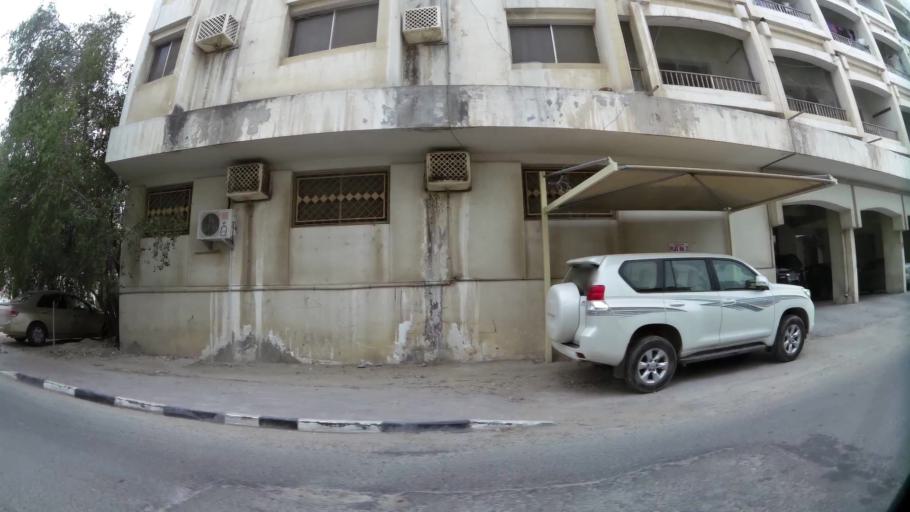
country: QA
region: Baladiyat ad Dawhah
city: Doha
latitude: 25.3017
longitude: 51.4942
